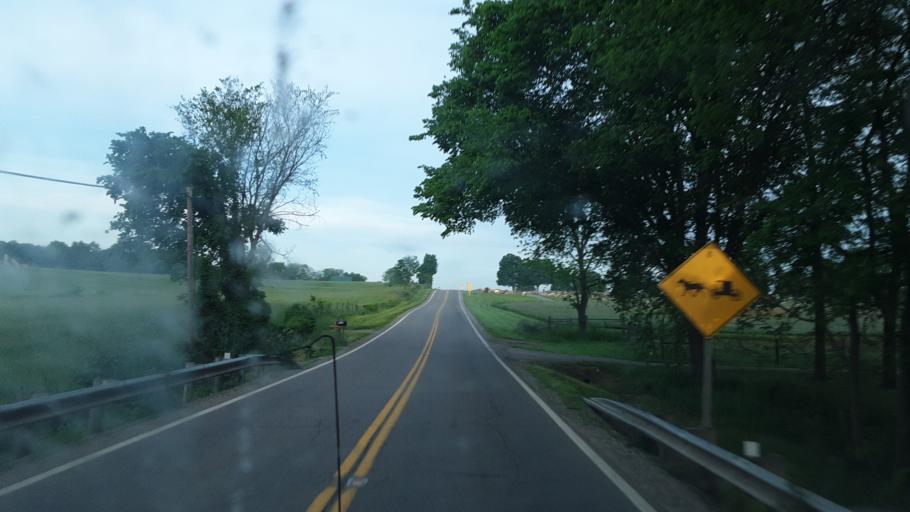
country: US
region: Ohio
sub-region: Ross County
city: Kingston
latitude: 39.4656
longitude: -82.7536
